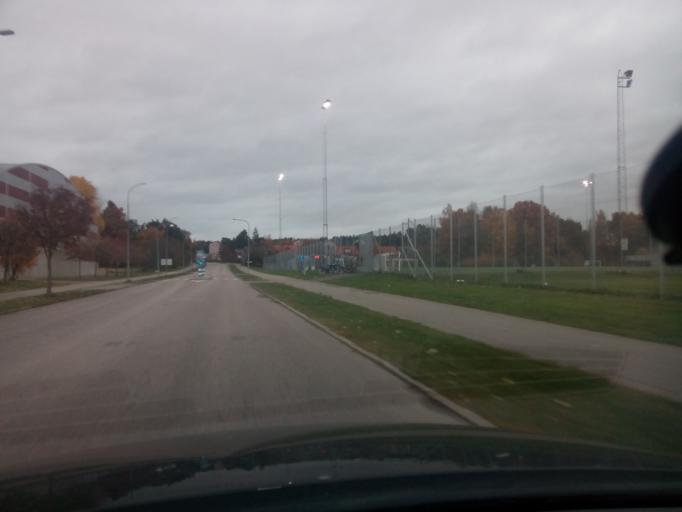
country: SE
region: Soedermanland
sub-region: Nykopings Kommun
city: Nykoping
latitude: 58.7485
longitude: 17.0429
